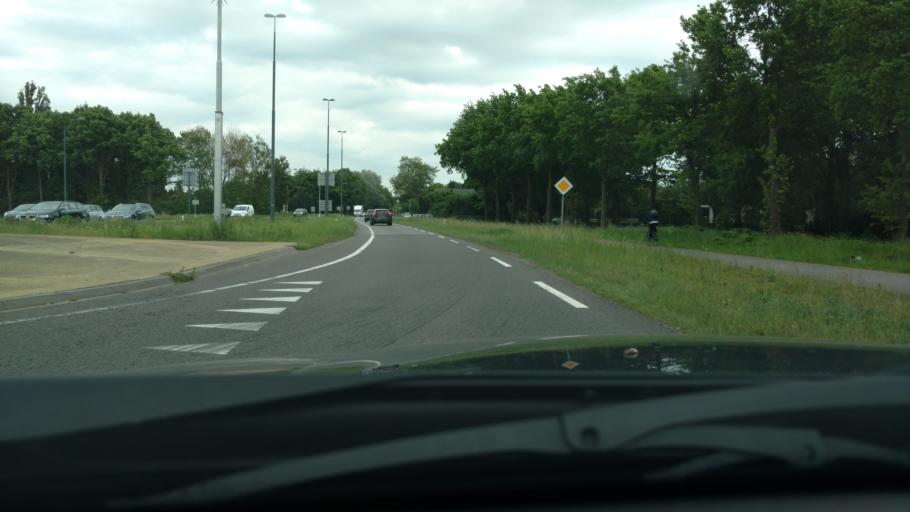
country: NL
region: Gelderland
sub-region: Gemeente Lochem
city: Epse
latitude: 52.2324
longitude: 6.1850
